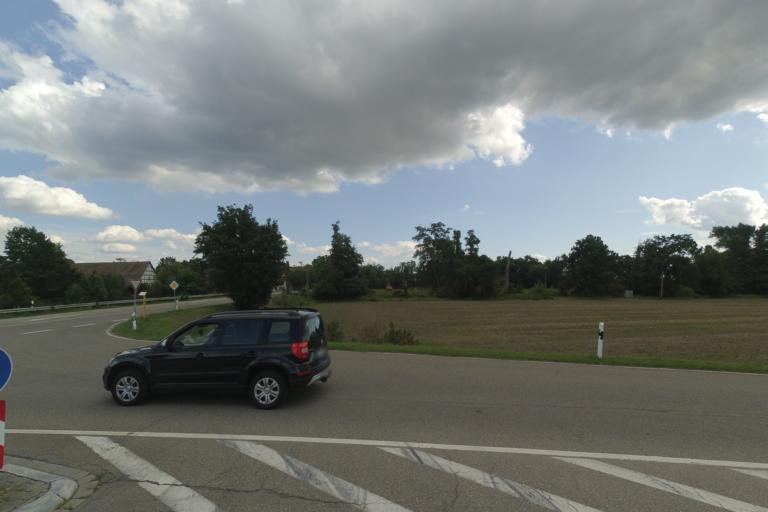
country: DE
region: Rheinland-Pfalz
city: Limburgerhof
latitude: 49.4086
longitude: 8.4050
